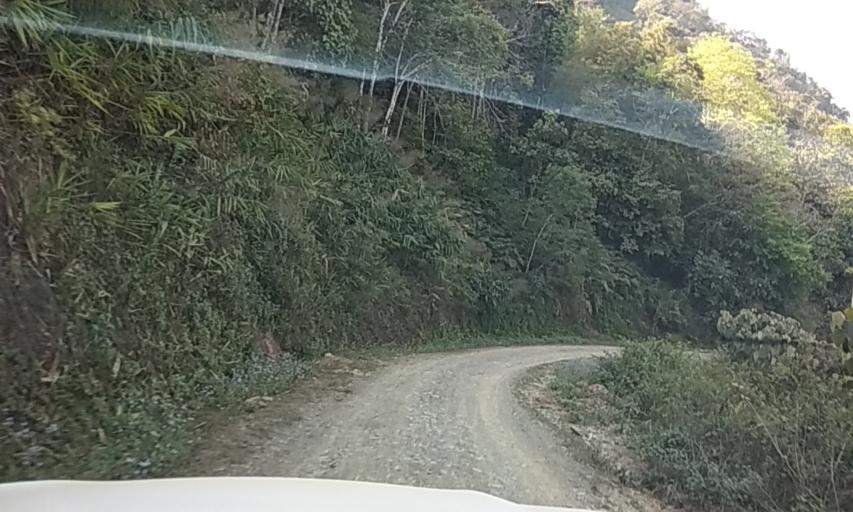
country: LA
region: Phongsali
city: Phongsali
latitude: 21.6966
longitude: 102.0762
